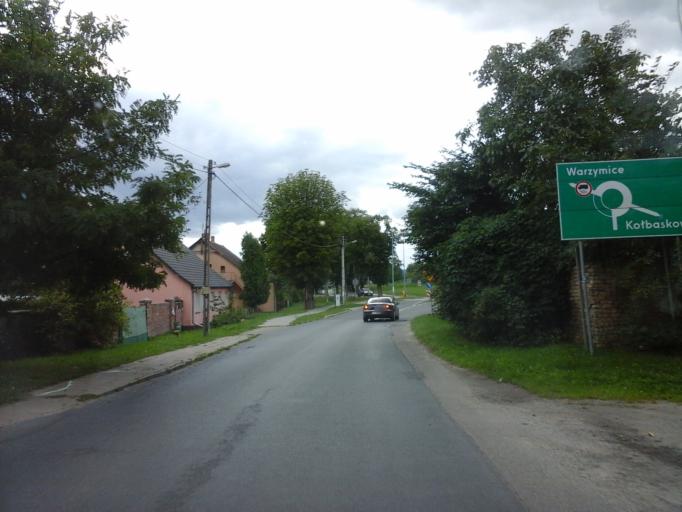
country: PL
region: West Pomeranian Voivodeship
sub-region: Powiat policki
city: Przeclaw
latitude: 53.3916
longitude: 14.4416
